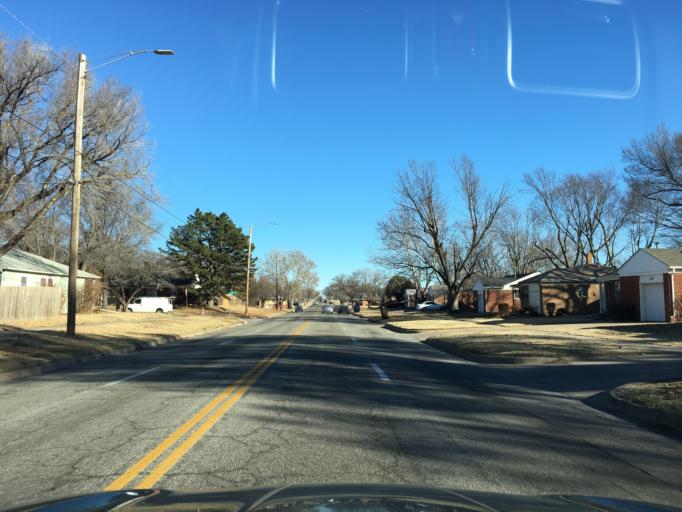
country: US
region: Kansas
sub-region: Sedgwick County
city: Wichita
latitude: 37.6719
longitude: -97.2666
